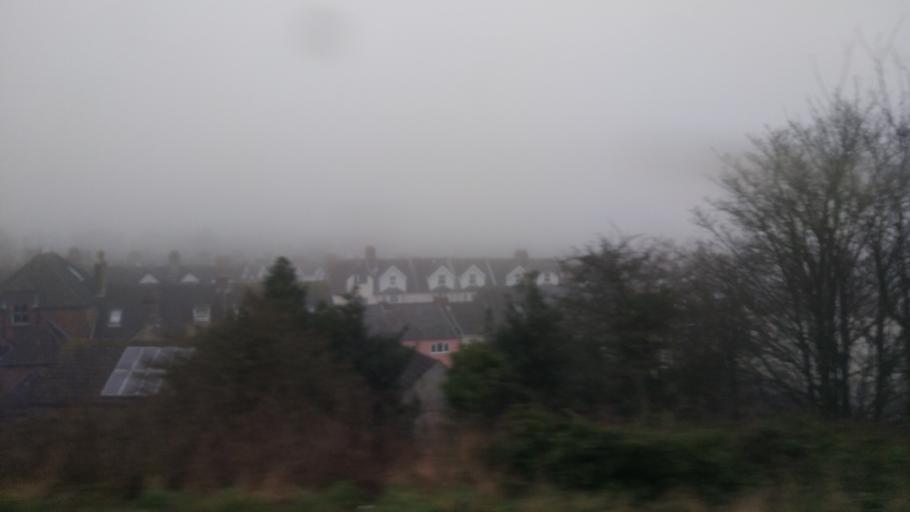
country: GB
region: England
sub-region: Kent
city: Folkestone
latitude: 51.0830
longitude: 1.1750
